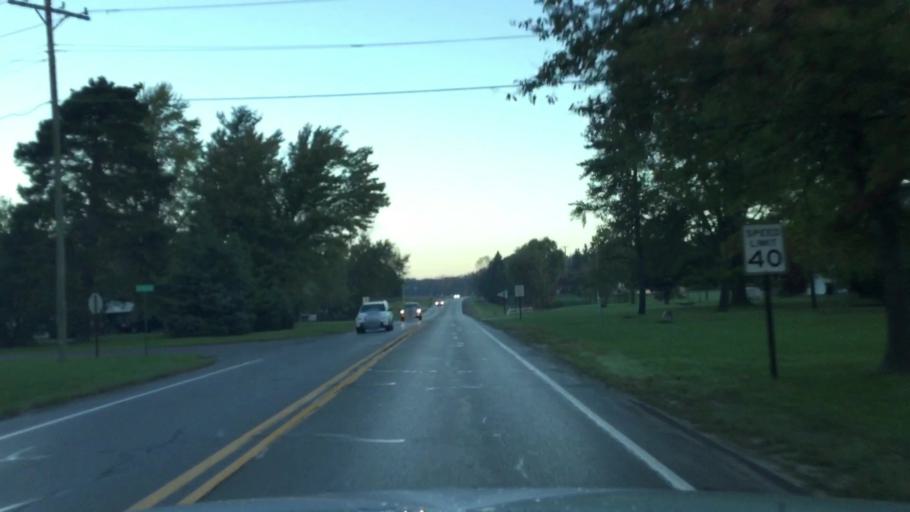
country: US
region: Michigan
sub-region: Livingston County
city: Howell
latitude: 42.6347
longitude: -83.9307
